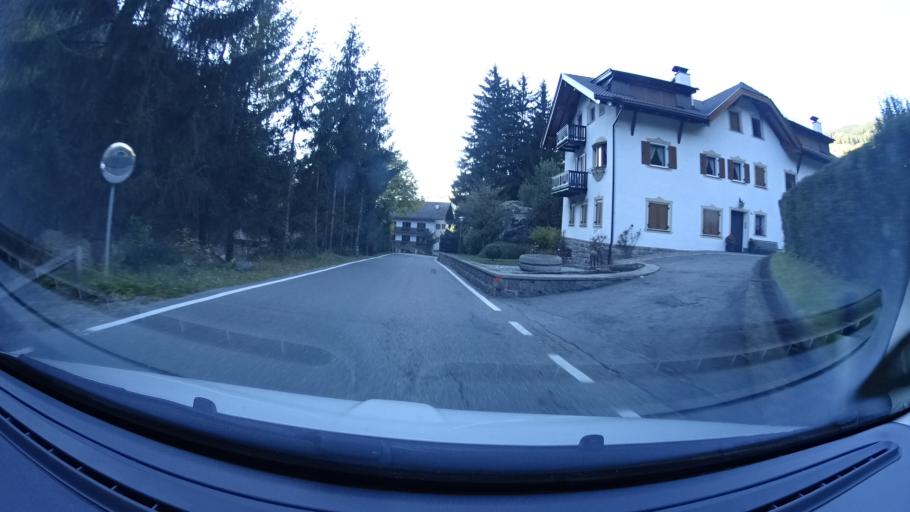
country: IT
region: Trentino-Alto Adige
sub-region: Bolzano
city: Ortisei
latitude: 46.5924
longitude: 11.6214
